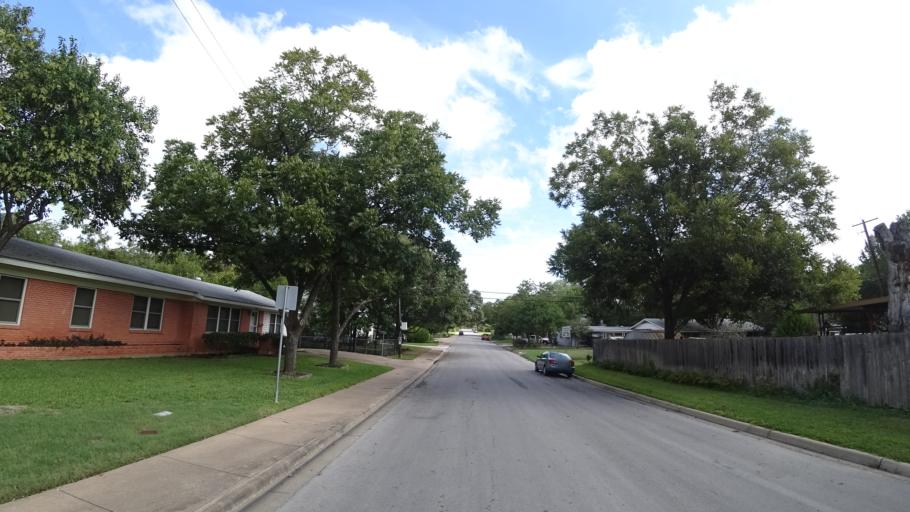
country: US
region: Texas
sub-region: Travis County
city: Austin
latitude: 30.3461
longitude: -97.7385
